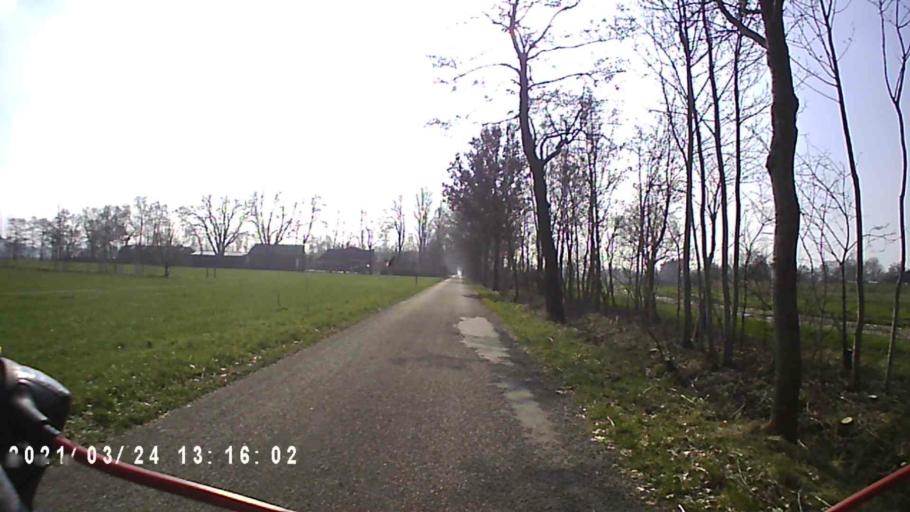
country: NL
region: Groningen
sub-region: Gemeente Leek
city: Leek
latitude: 53.1138
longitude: 6.2903
